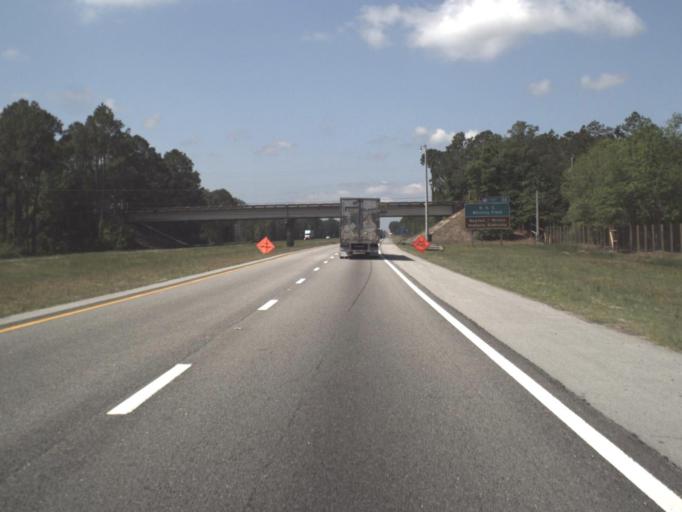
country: US
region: Florida
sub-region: Santa Rosa County
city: Bagdad
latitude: 30.5803
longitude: -87.0183
